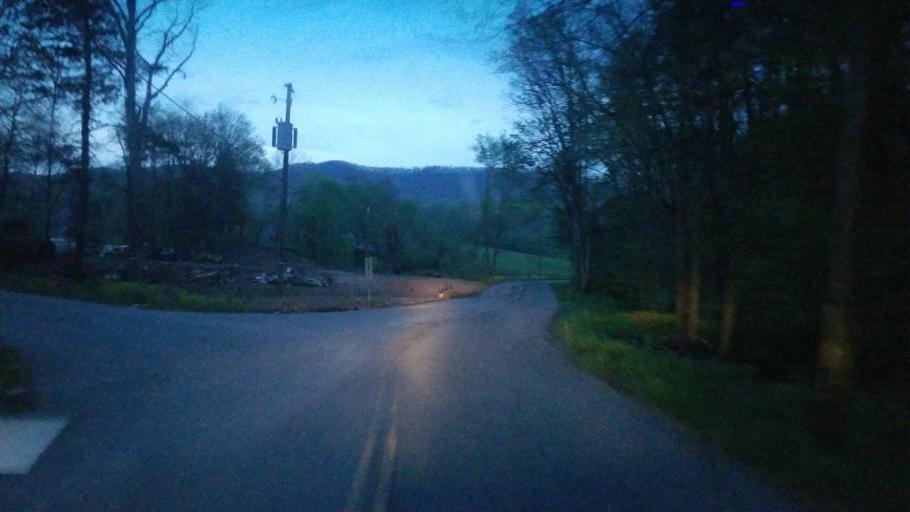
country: US
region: Virginia
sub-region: Smyth County
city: Atkins
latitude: 36.8378
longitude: -81.4550
